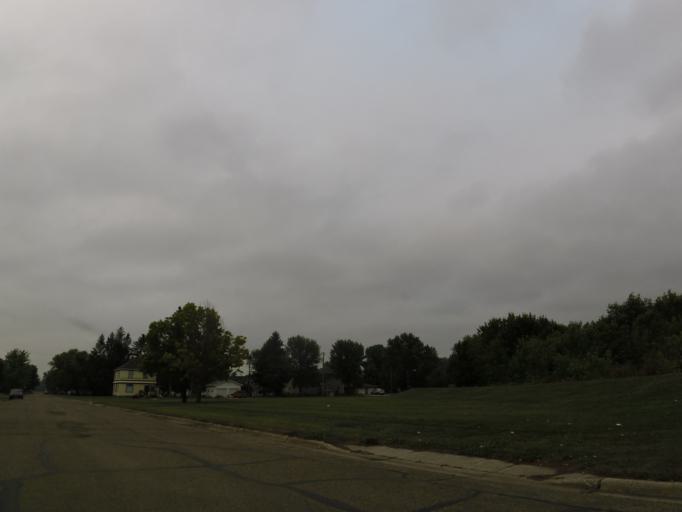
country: US
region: North Dakota
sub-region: Walsh County
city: Grafton
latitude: 48.5642
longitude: -97.1763
